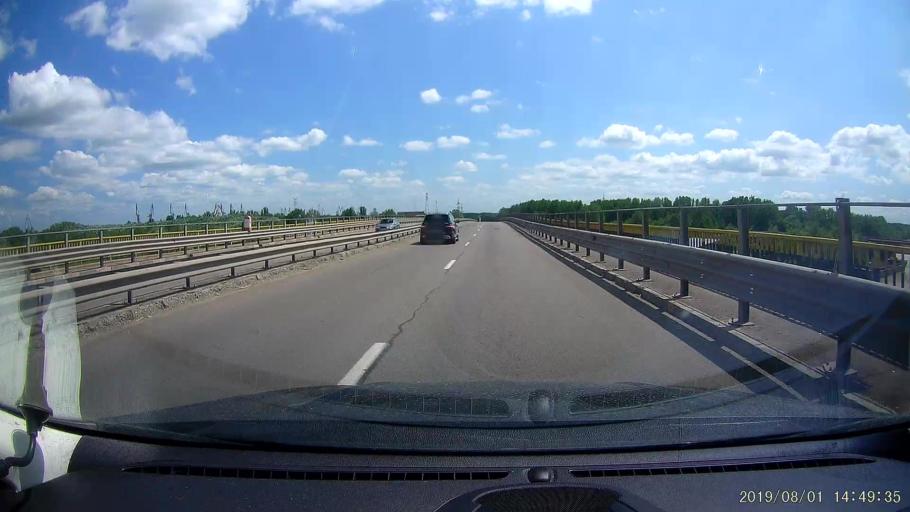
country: RO
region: Galati
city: Galati
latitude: 45.4018
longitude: 28.0153
